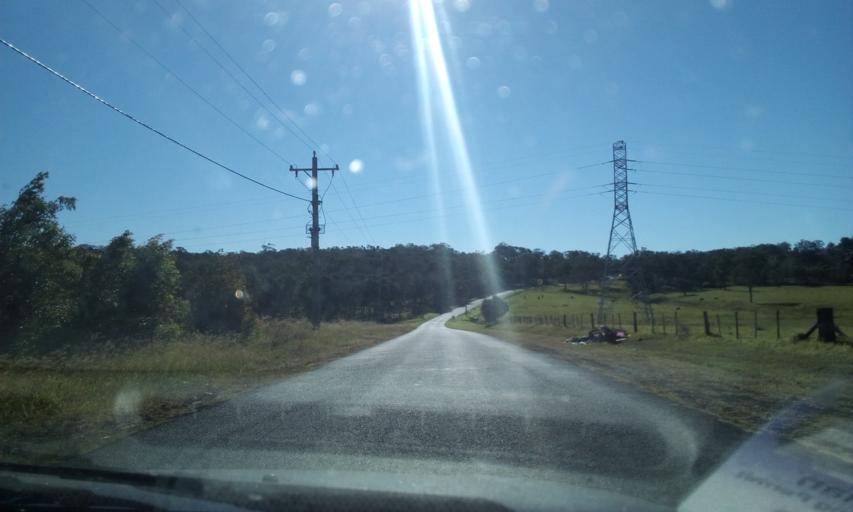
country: AU
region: New South Wales
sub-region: Wollongong
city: Dapto
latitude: -34.5231
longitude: 150.7787
